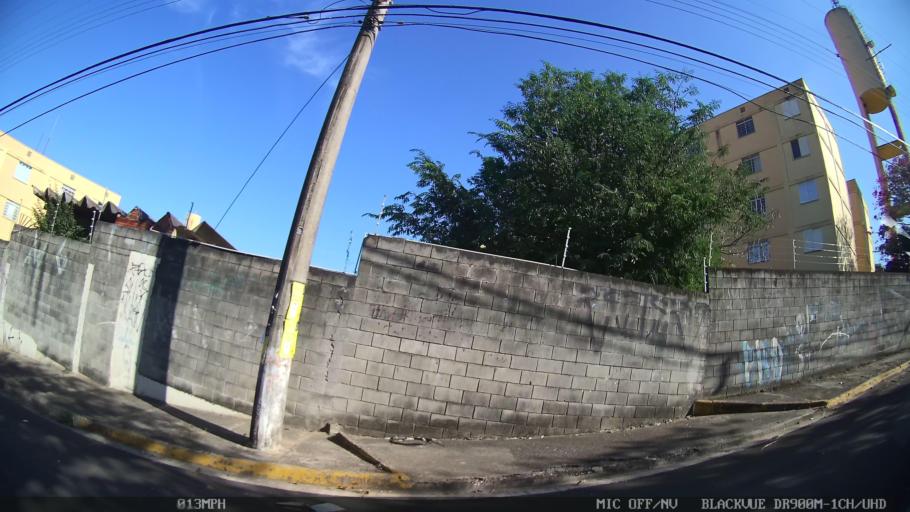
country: BR
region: Sao Paulo
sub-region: Campinas
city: Campinas
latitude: -22.9501
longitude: -47.1203
